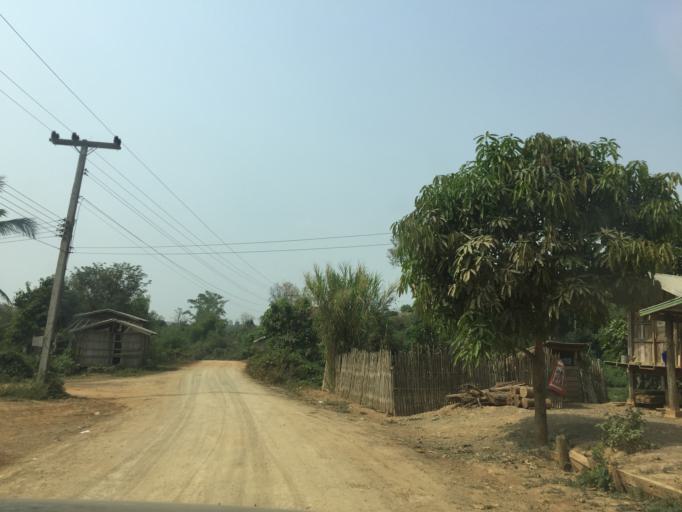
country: TH
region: Uttaradit
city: Ban Khok
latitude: 17.9483
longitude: 101.2832
